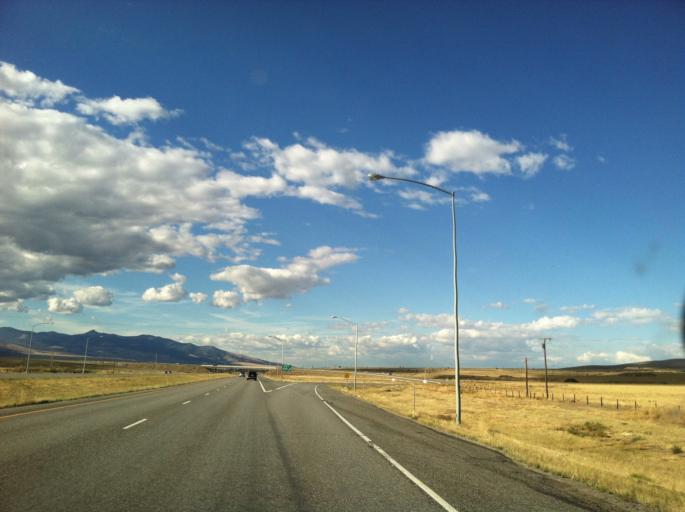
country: US
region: Montana
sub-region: Deer Lodge County
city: Warm Springs
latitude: 46.0902
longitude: -112.7907
